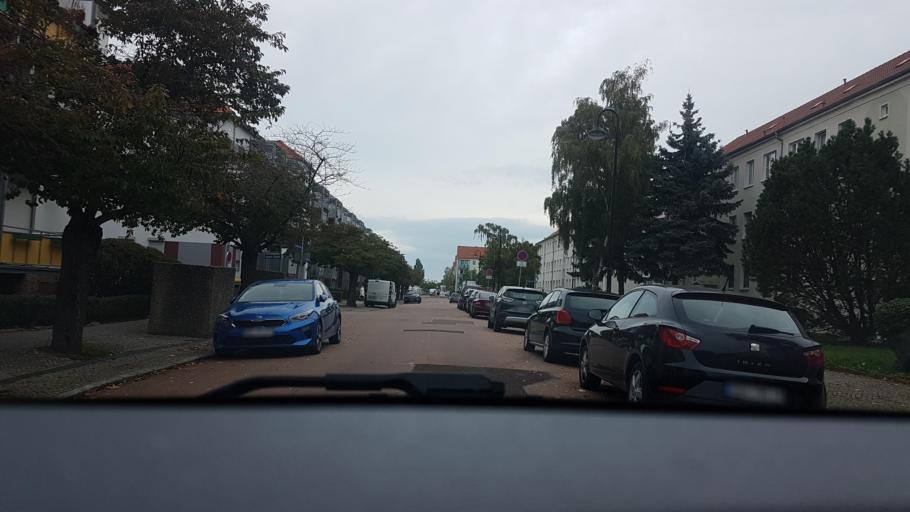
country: DE
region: Saxony-Anhalt
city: Bernburg
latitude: 51.7861
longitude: 11.7459
